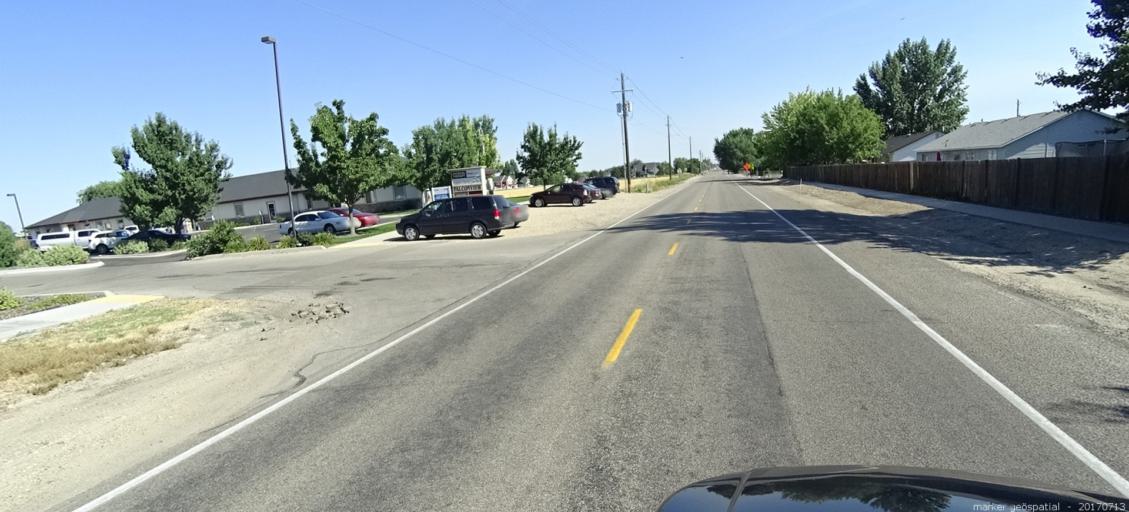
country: US
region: Idaho
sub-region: Ada County
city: Kuna
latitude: 43.4970
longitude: -116.4137
